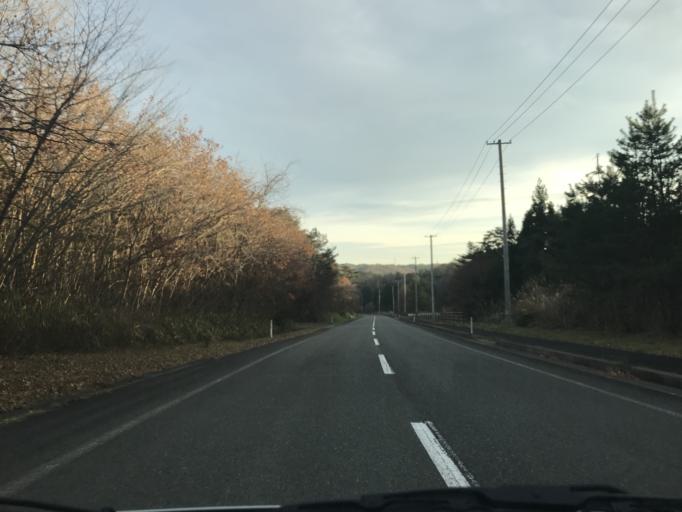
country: JP
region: Iwate
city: Ichinoseki
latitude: 38.9794
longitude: 141.0709
